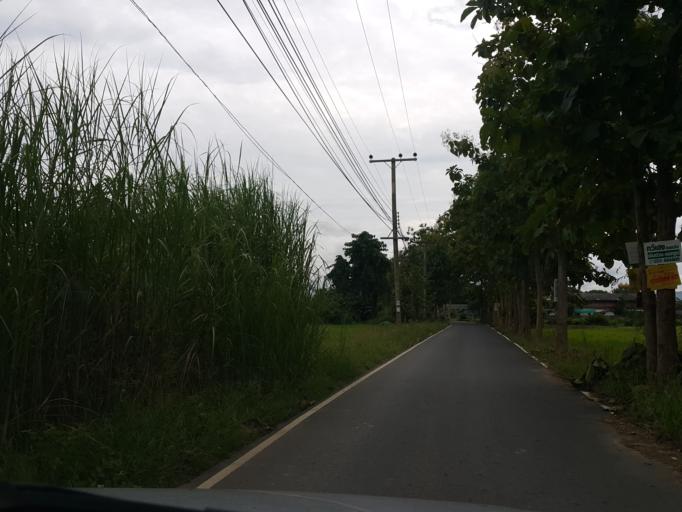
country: TH
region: Chiang Mai
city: San Sai
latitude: 18.8415
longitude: 99.1268
